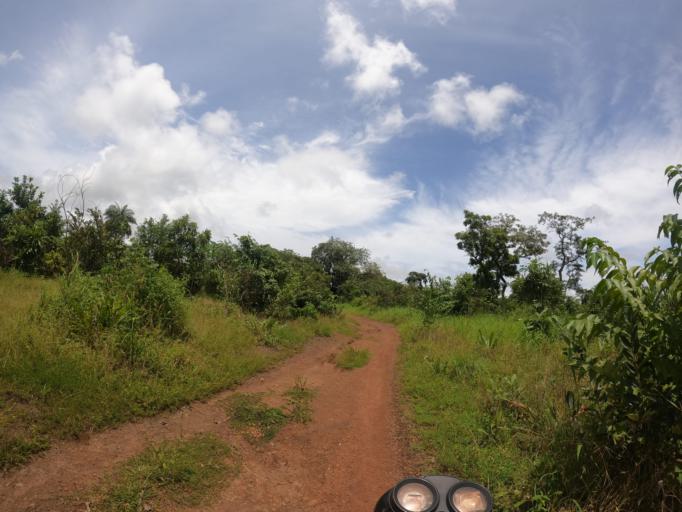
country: SL
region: Northern Province
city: Binkolo
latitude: 9.1454
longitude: -12.2440
